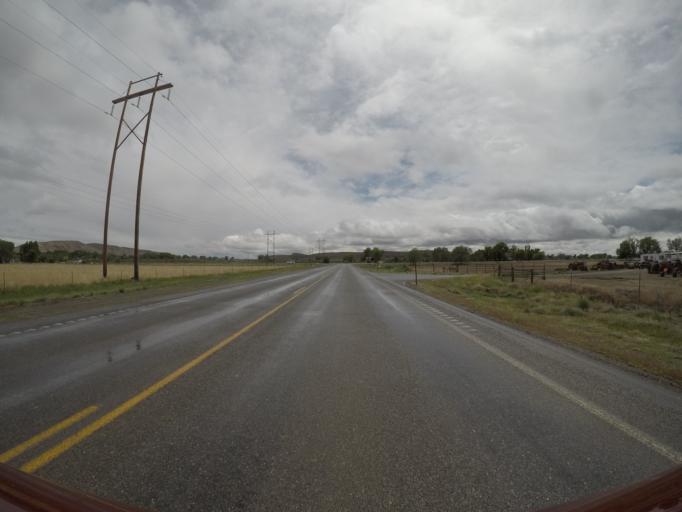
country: US
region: Wyoming
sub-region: Big Horn County
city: Lovell
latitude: 44.8423
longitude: -108.3316
